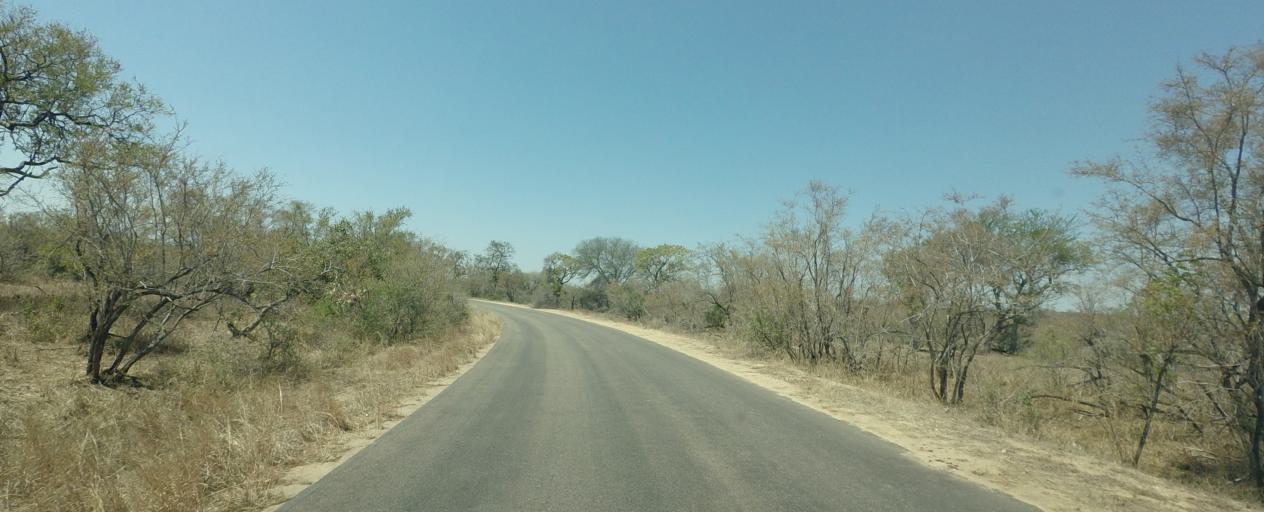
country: ZA
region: Limpopo
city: Thulamahashi
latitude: -24.4408
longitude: 31.4880
